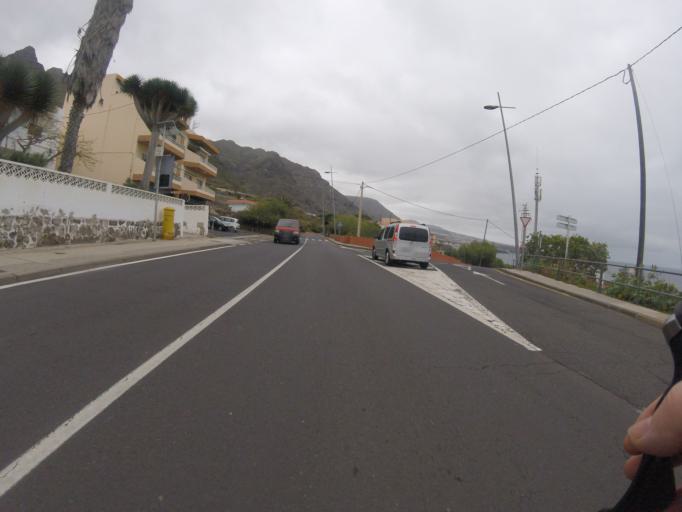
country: ES
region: Canary Islands
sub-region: Provincia de Santa Cruz de Tenerife
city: Tegueste
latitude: 28.5677
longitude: -16.3284
